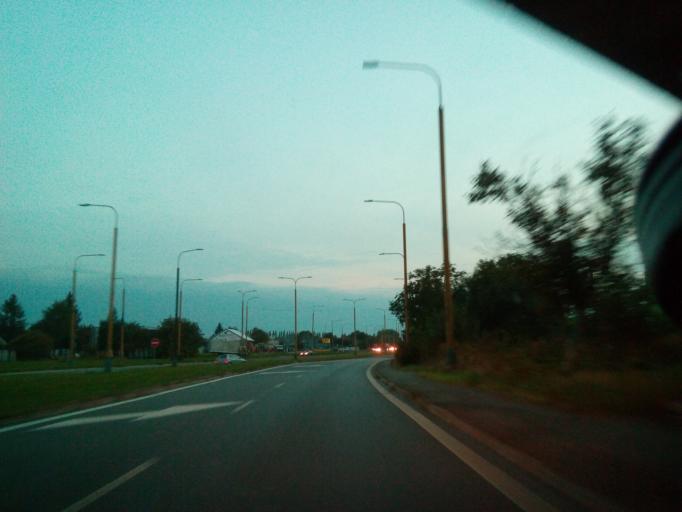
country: SK
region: Presovsky
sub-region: Okres Presov
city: Presov
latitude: 49.0145
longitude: 21.2671
